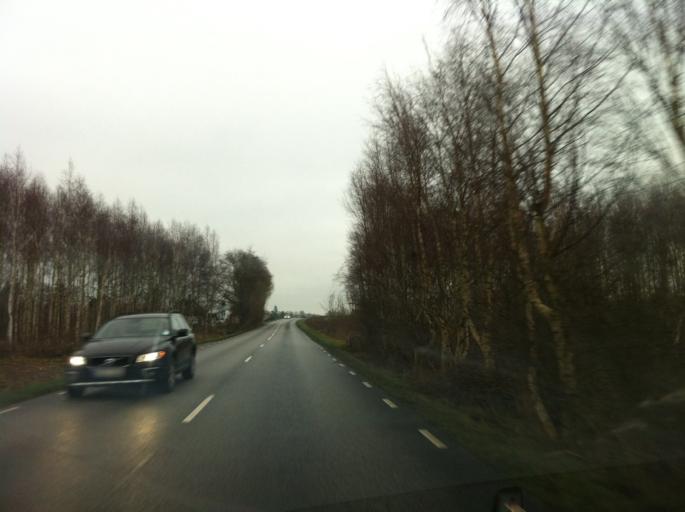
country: SE
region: Skane
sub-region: Hoors Kommun
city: Loberod
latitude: 55.7435
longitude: 13.4173
